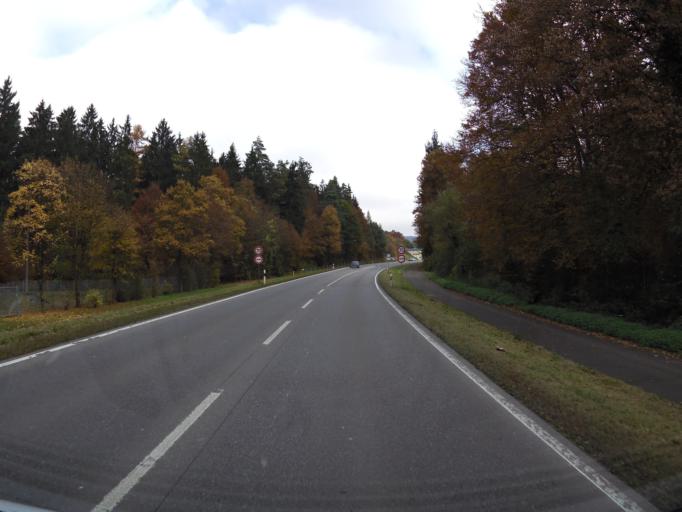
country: DE
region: Baden-Wuerttemberg
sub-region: Freiburg Region
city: Radolfzell am Bodensee
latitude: 47.7607
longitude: 8.9805
